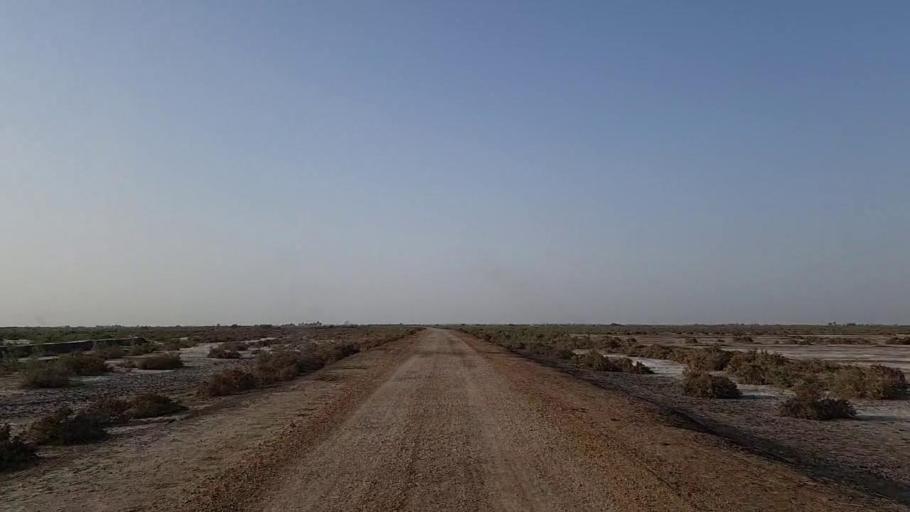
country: PK
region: Sindh
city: Jati
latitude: 24.3572
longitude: 68.1475
